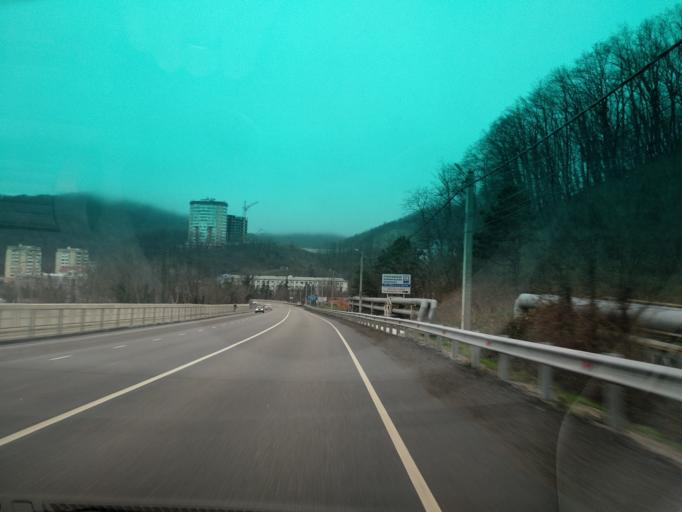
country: RU
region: Krasnodarskiy
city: Tuapse
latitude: 44.1143
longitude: 39.0696
